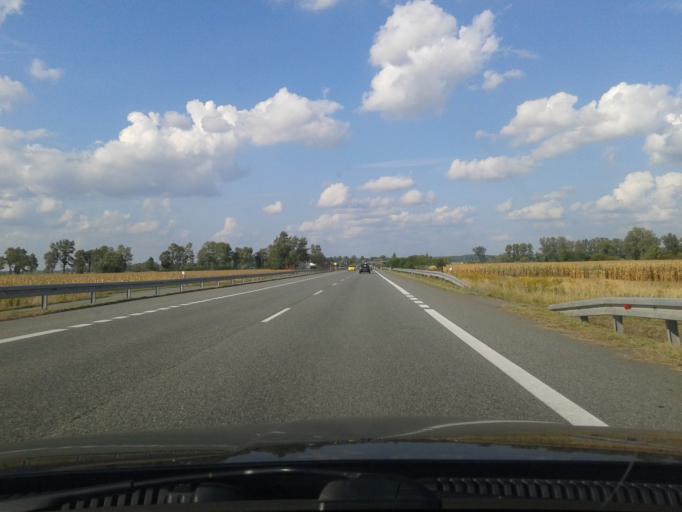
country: PL
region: Silesian Voivodeship
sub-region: Powiat wodzislawski
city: Olza
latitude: 49.9454
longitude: 18.3268
